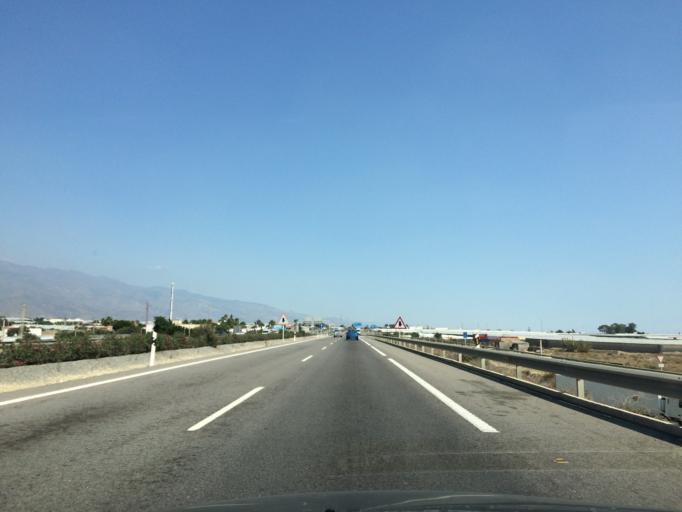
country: ES
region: Andalusia
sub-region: Provincia de Almeria
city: El Ejido
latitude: 36.7619
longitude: -2.8622
